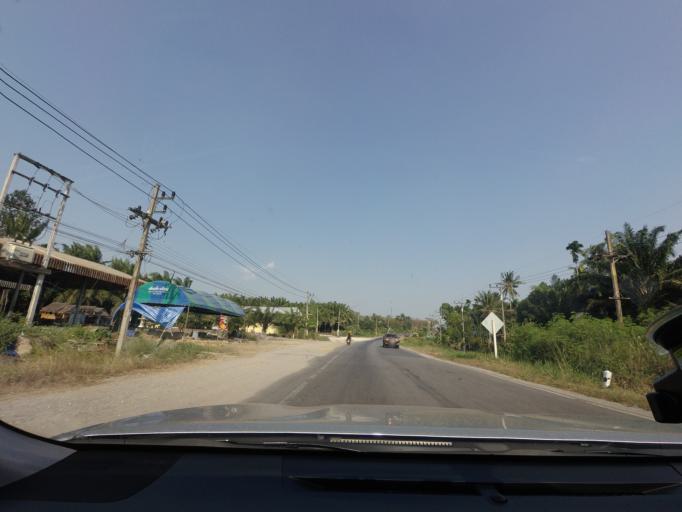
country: TH
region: Surat Thani
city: Phrasaeng
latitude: 8.5607
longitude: 99.1501
